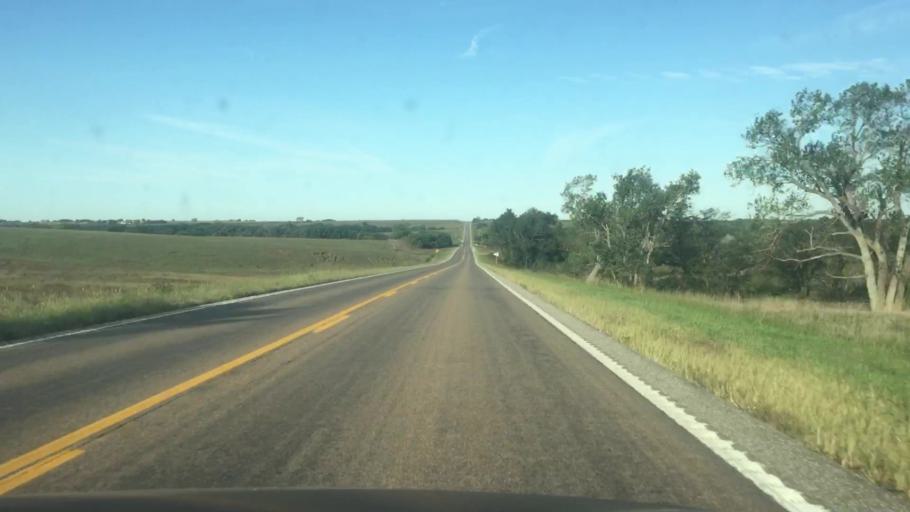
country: US
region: Nebraska
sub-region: Thayer County
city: Hebron
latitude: 40.1473
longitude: -97.5111
